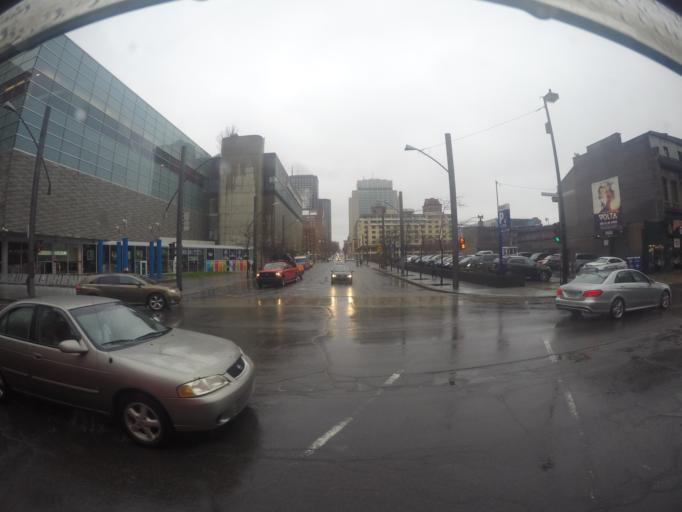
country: CA
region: Quebec
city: Montreal-Ouest
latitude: 45.4109
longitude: -73.6589
